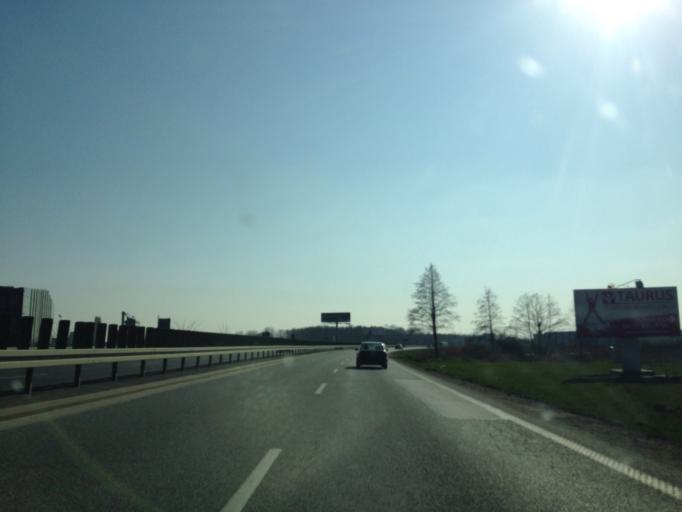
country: PL
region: Lower Silesian Voivodeship
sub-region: Powiat wroclawski
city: Dlugoleka
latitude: 51.1871
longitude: 17.2263
